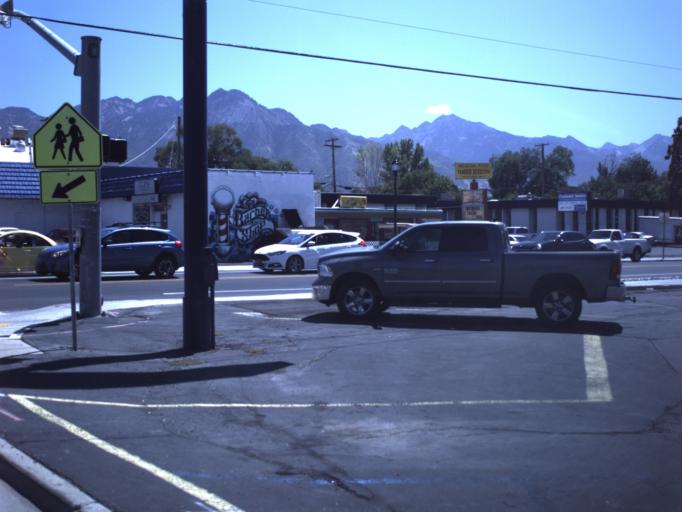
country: US
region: Utah
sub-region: Salt Lake County
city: Millcreek
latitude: 40.6998
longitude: -111.8658
